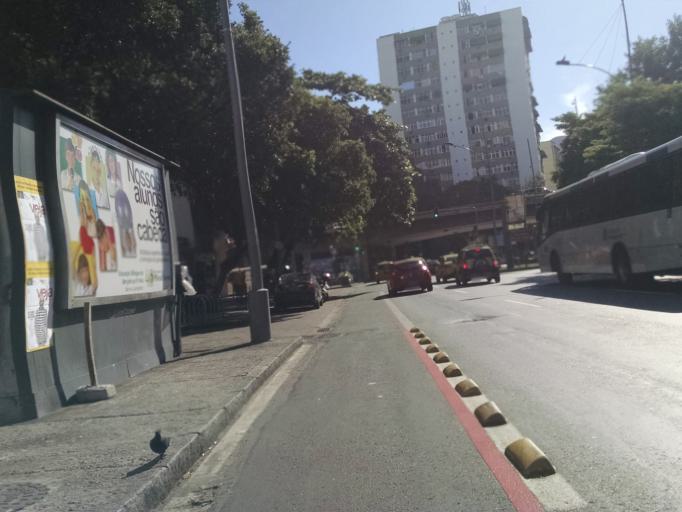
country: BR
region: Rio de Janeiro
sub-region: Rio De Janeiro
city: Rio de Janeiro
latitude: -22.9330
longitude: -43.1840
